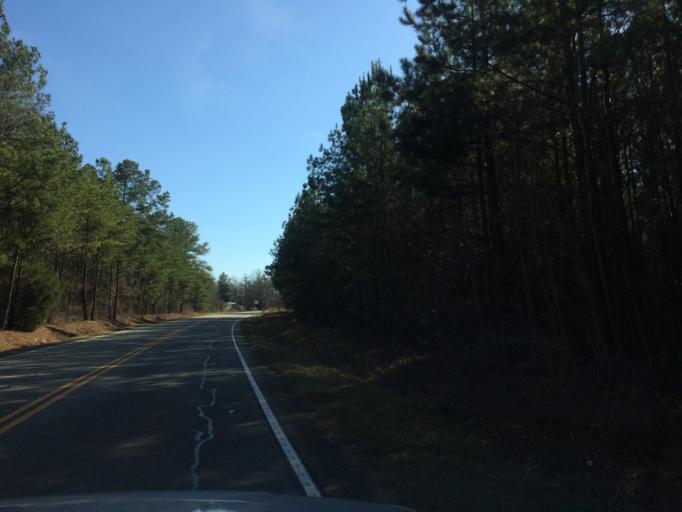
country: US
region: South Carolina
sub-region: Greenwood County
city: Ninety Six
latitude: 34.3163
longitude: -82.0506
